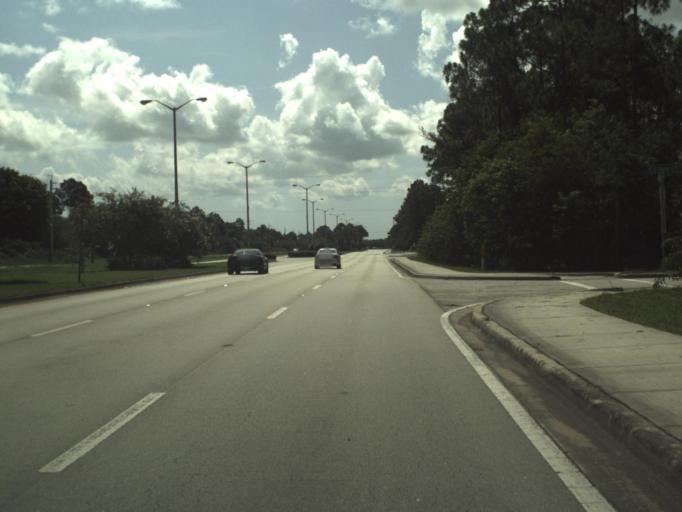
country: US
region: Florida
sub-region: Saint Lucie County
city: Port Saint Lucie
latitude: 27.2607
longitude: -80.3825
